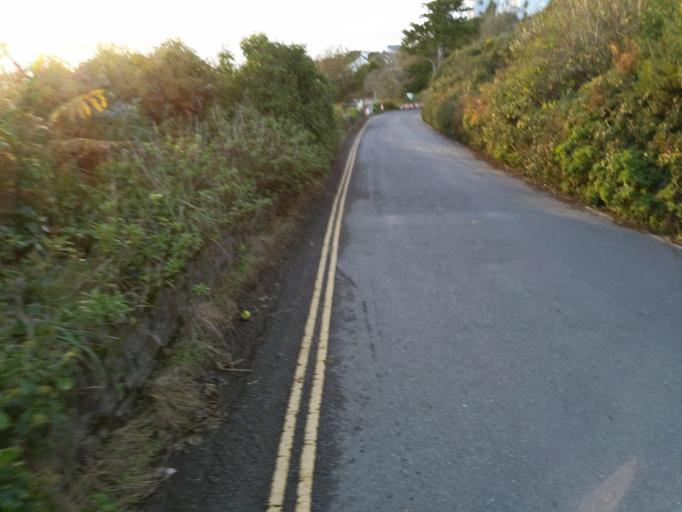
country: GB
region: England
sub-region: Cornwall
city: Looe
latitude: 50.3614
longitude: -4.3594
